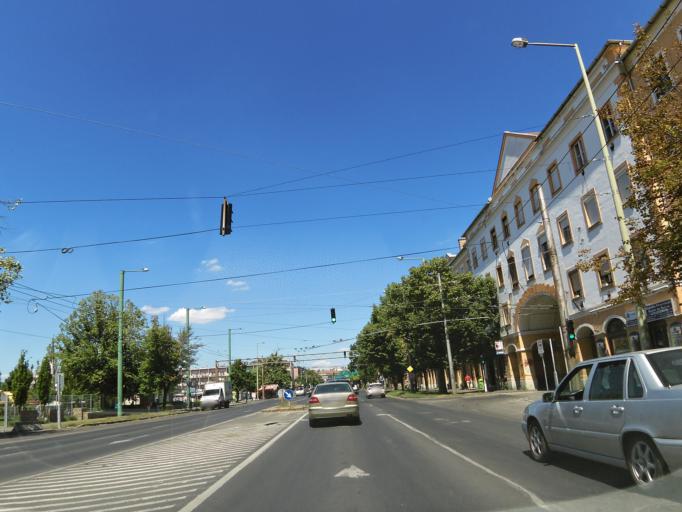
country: HU
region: Csongrad
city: Szeged
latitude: 46.2556
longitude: 20.1405
